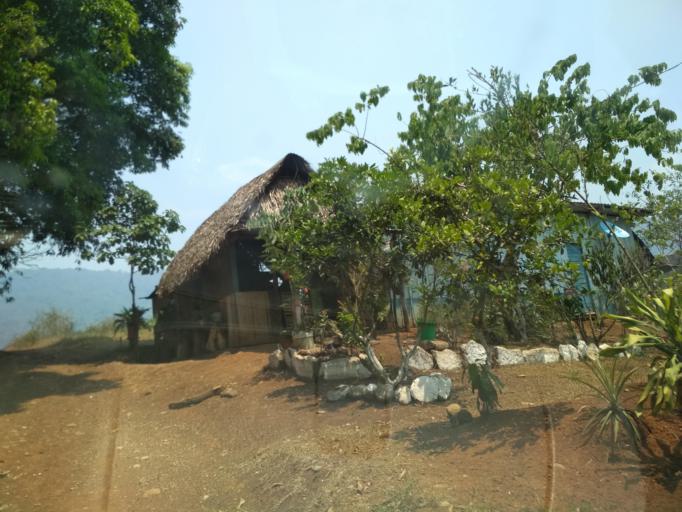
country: MX
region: Veracruz
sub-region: Tezonapa
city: Laguna Chica (Pueblo Nuevo)
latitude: 18.5593
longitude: -96.7261
